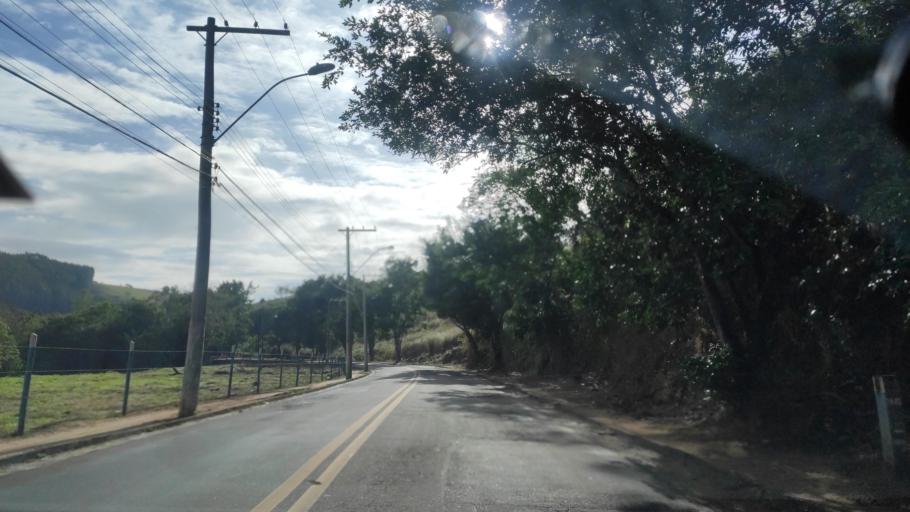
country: BR
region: Espirito Santo
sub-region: Nova Venecia
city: Nova Venecia
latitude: -18.7161
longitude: -40.3869
